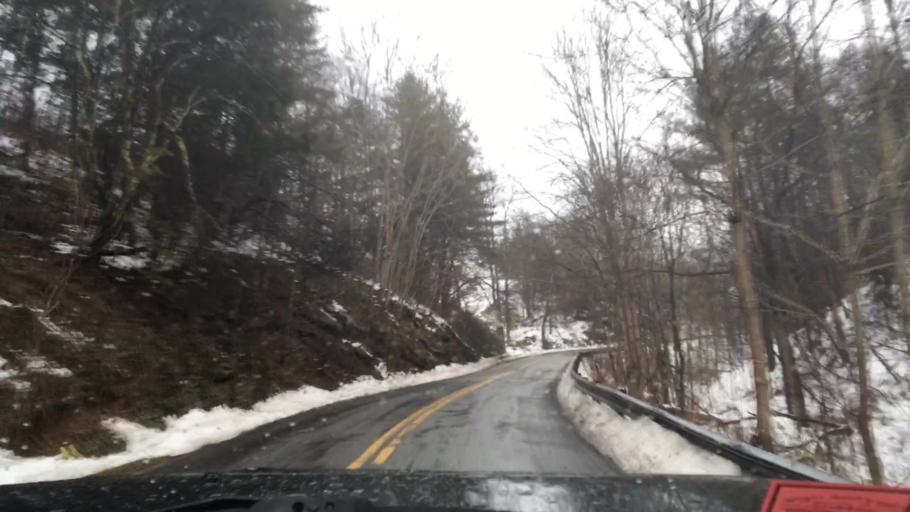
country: US
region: Virginia
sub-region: Pulaski County
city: Dublin
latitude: 37.0036
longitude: -80.6708
